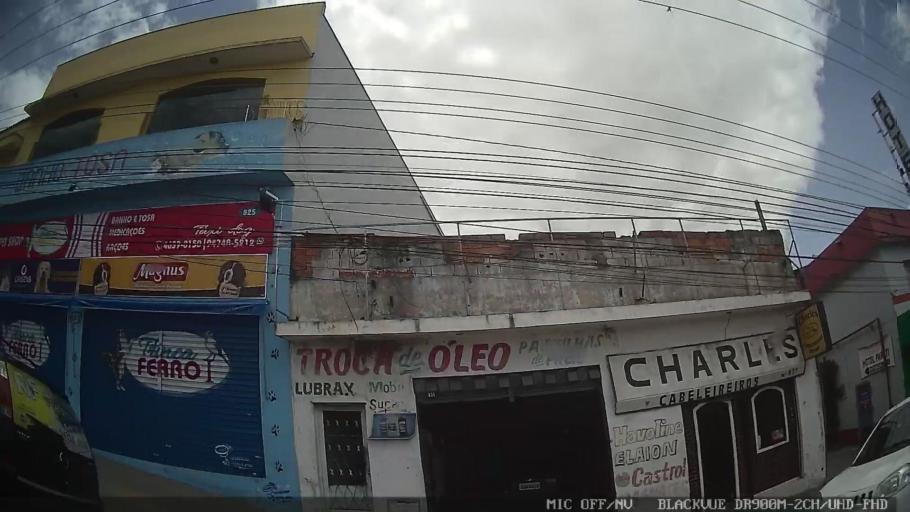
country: BR
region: Sao Paulo
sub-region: Poa
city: Poa
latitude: -23.5351
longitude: -46.3541
